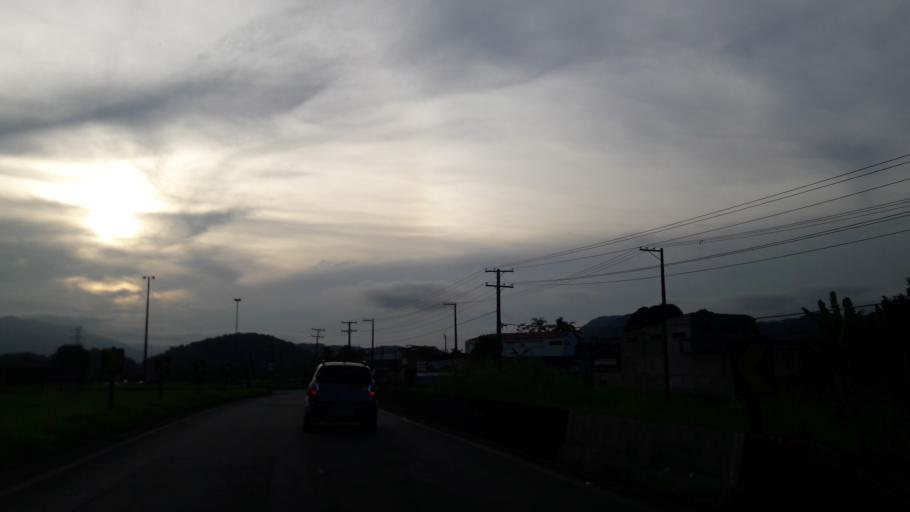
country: BR
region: Sao Paulo
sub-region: Peruibe
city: Peruibe
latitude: -24.2921
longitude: -47.0267
